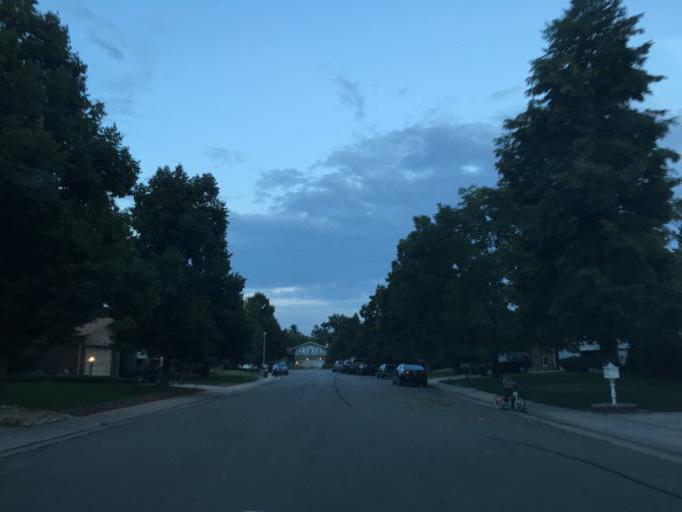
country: US
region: Colorado
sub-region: Adams County
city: Aurora
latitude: 39.6872
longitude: -104.8495
